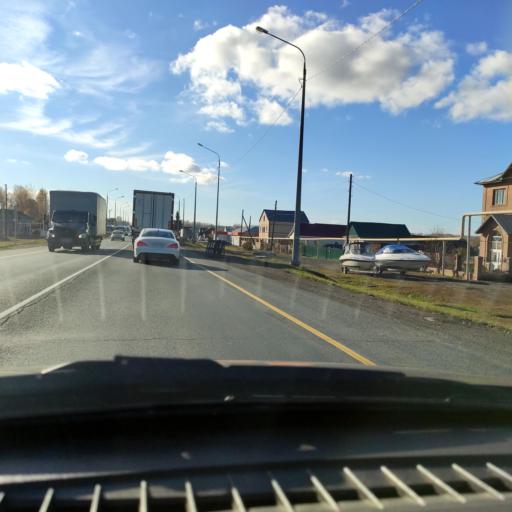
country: RU
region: Samara
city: Zhigulevsk
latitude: 53.3251
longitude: 49.4084
